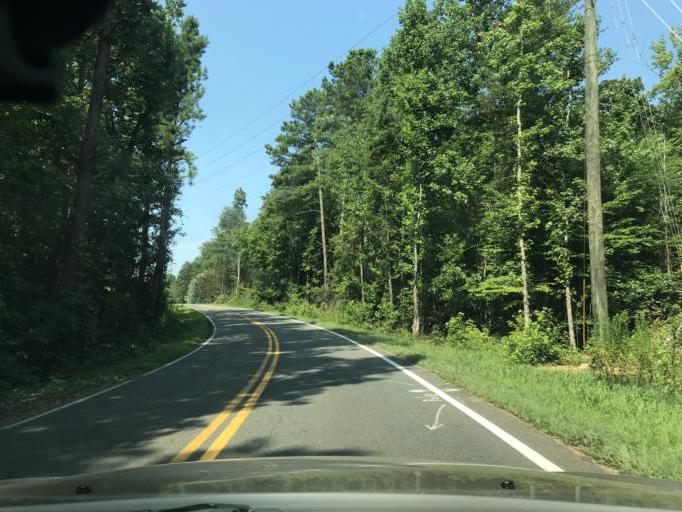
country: US
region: Georgia
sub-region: Hall County
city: Flowery Branch
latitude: 34.2319
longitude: -84.0026
